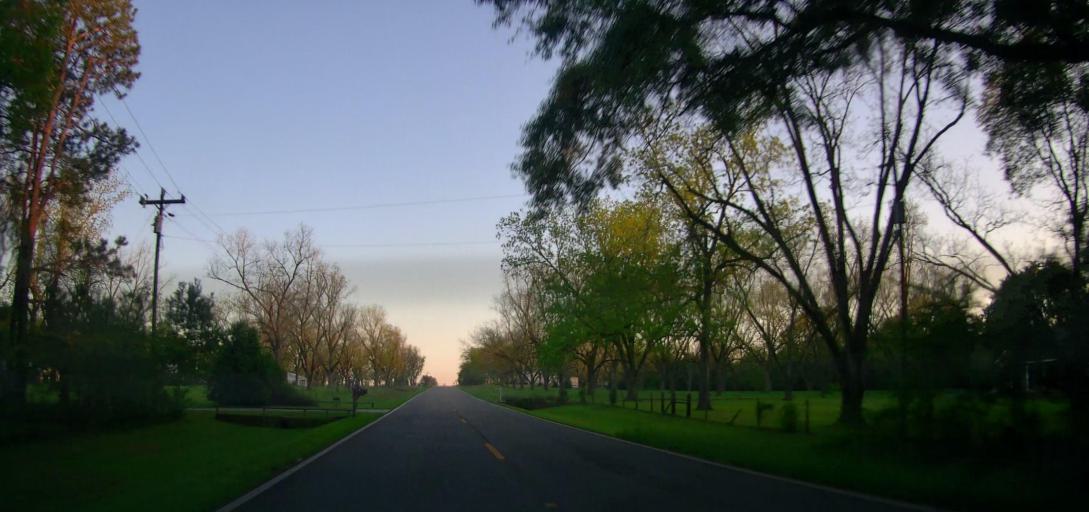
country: US
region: Georgia
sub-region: Ben Hill County
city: Fitzgerald
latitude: 31.7219
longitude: -83.3098
